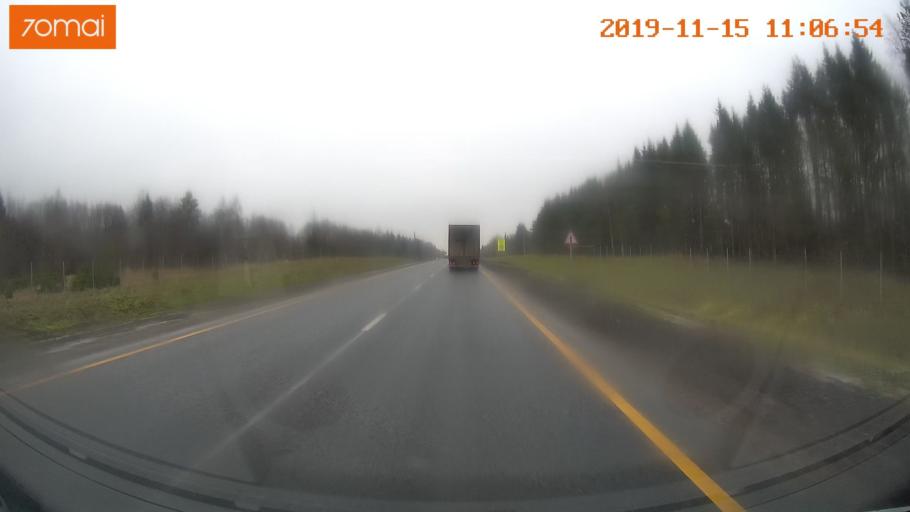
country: RU
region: Vologda
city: Chebsara
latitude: 59.1190
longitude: 39.0382
